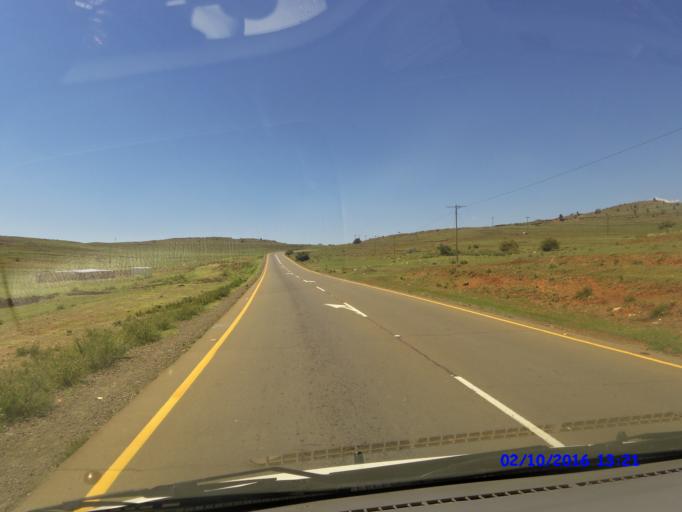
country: LS
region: Maseru
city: Nako
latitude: -29.4220
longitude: 27.7088
